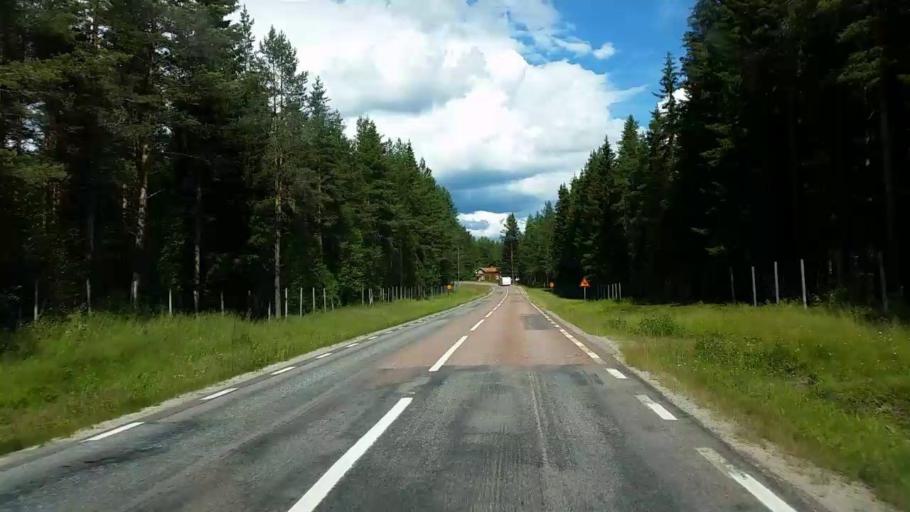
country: SE
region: Gaevleborg
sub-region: Ovanakers Kommun
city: Edsbyn
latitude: 61.3029
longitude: 15.5080
